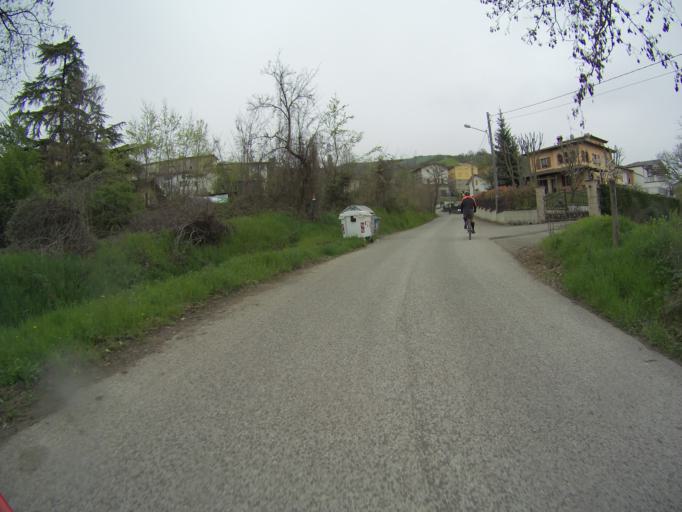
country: IT
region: Emilia-Romagna
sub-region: Provincia di Reggio Emilia
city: Ciano d'Enza
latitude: 44.5918
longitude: 10.4056
